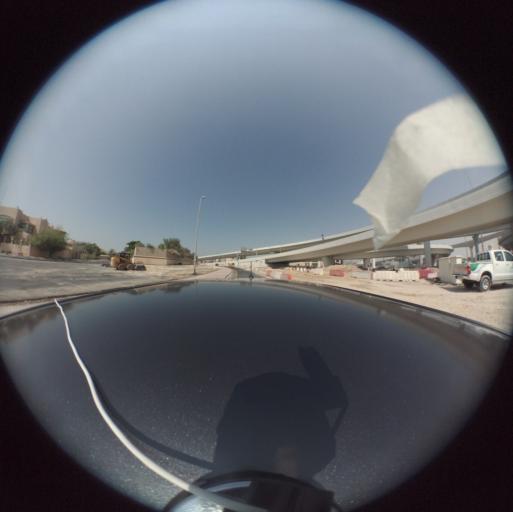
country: AE
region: Dubai
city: Dubai
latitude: 25.1646
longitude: 55.2337
